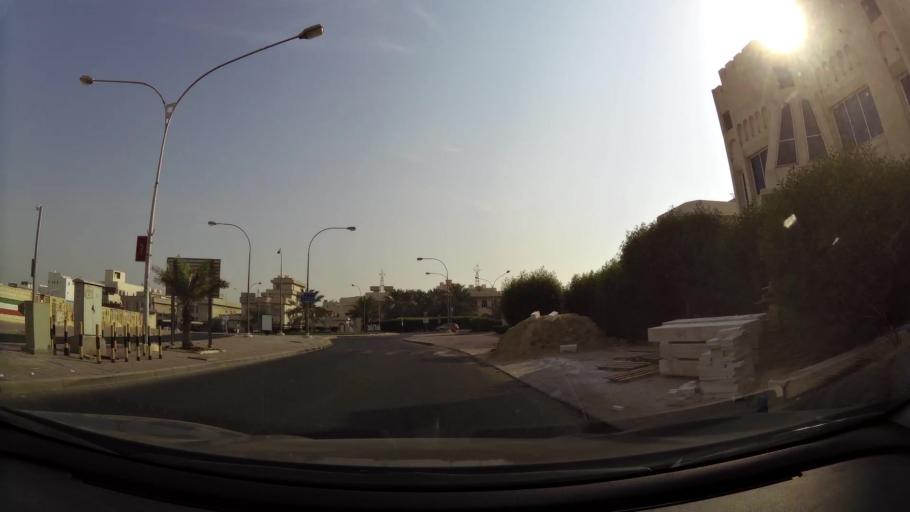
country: KW
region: Al Farwaniyah
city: Al Farwaniyah
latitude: 29.3108
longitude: 47.9842
